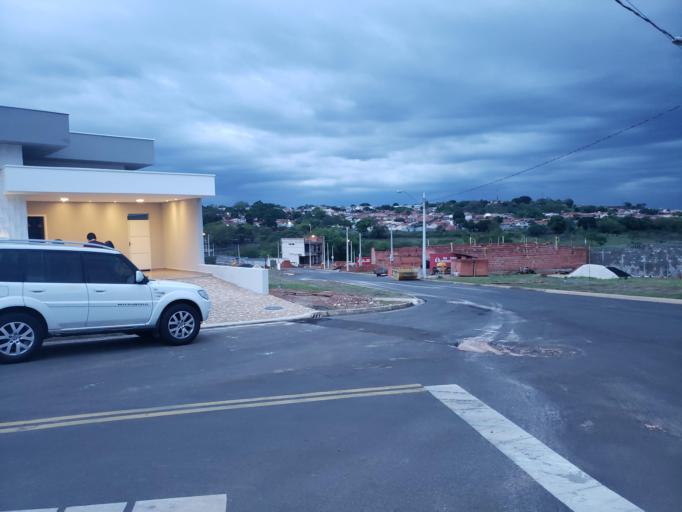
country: BR
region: Sao Paulo
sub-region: Moji-Guacu
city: Mogi-Gaucu
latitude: -22.3935
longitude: -46.9538
